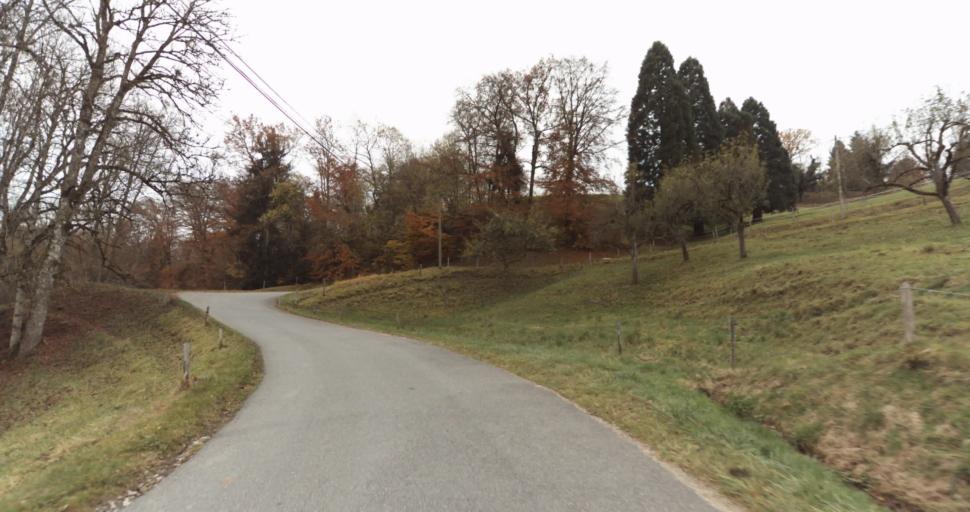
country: FR
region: Rhone-Alpes
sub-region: Departement de la Haute-Savoie
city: Chavanod
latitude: 45.8755
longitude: 6.0373
